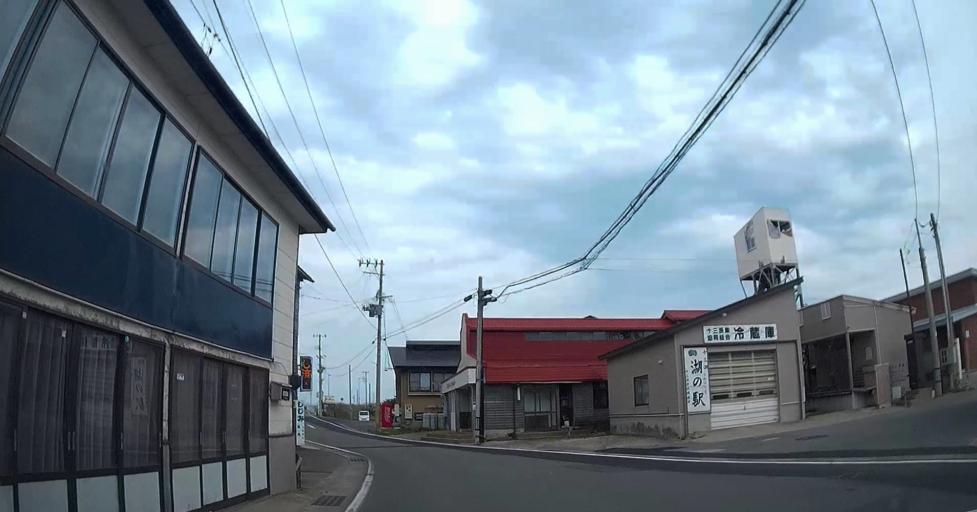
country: JP
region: Aomori
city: Shimokizukuri
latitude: 41.0363
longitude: 140.3294
